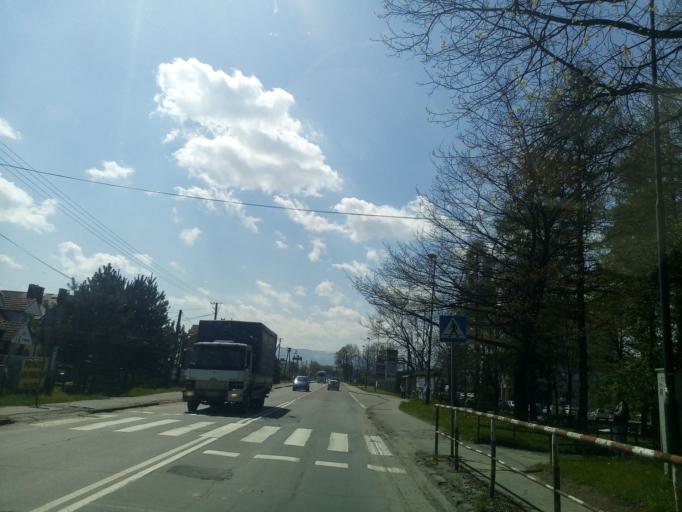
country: PL
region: Lesser Poland Voivodeship
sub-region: Powiat nowosadecki
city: Nowy Sacz
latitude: 49.5926
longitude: 20.6788
